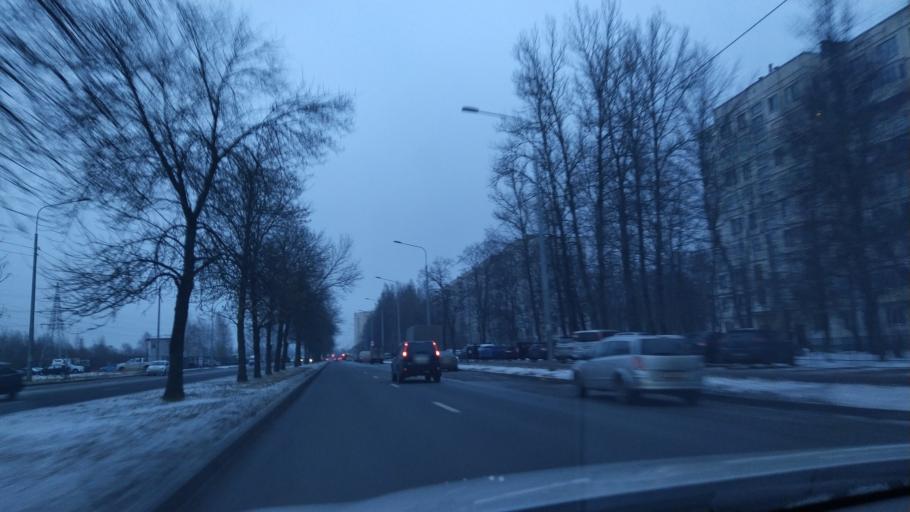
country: RU
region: St.-Petersburg
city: Grazhdanka
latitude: 60.0178
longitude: 30.4226
